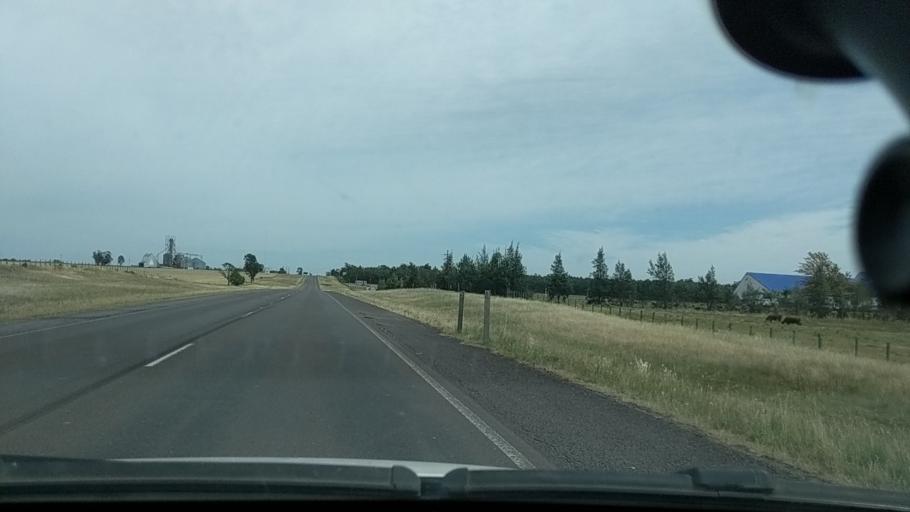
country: UY
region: Durazno
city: Durazno
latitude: -33.4550
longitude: -56.4688
